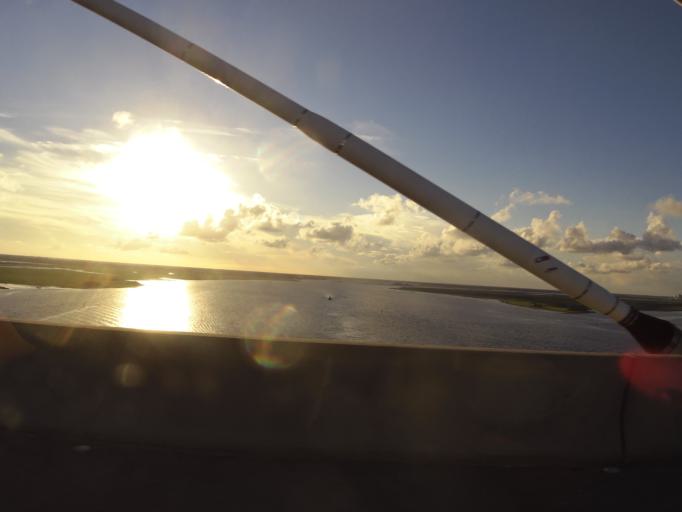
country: US
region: Georgia
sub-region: Glynn County
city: Brunswick
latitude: 31.1162
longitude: -81.4852
